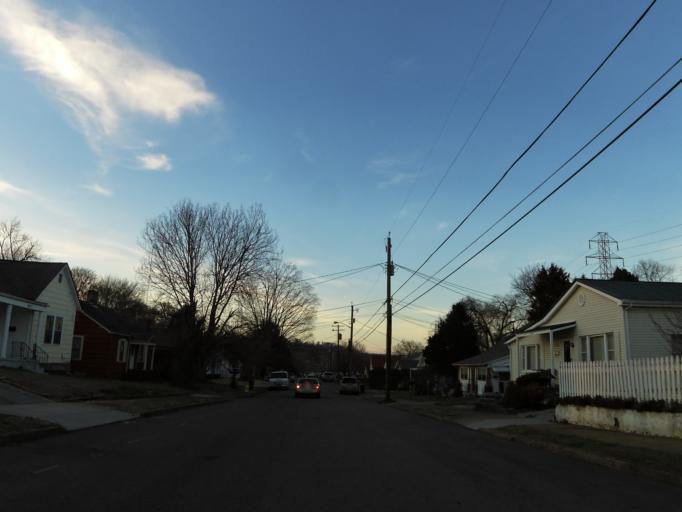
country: US
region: Tennessee
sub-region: Knox County
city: Knoxville
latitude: 35.9993
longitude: -83.9171
